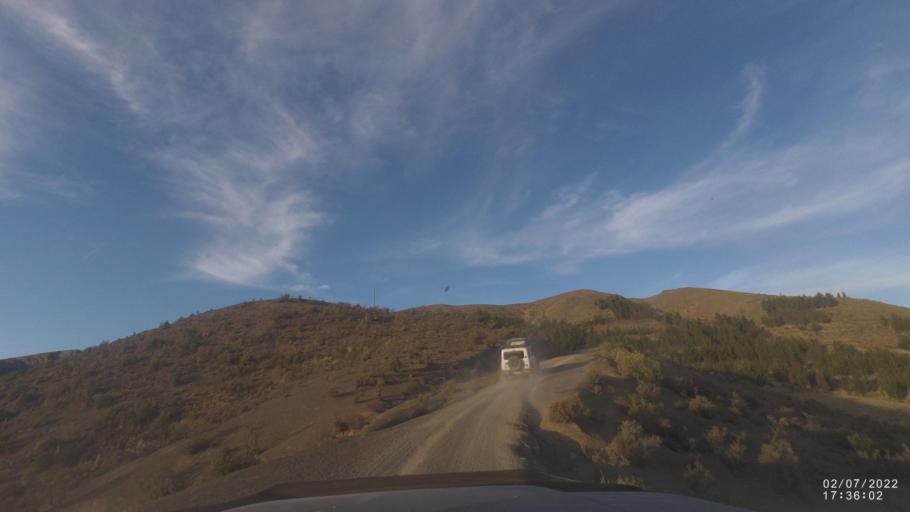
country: BO
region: Cochabamba
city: Irpa Irpa
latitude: -17.8766
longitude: -66.6211
